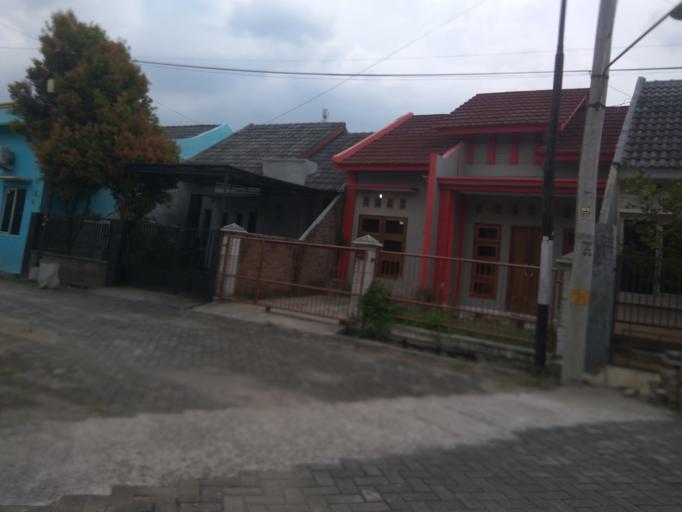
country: ID
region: Central Java
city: Semarang
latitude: -7.0671
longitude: 110.4445
